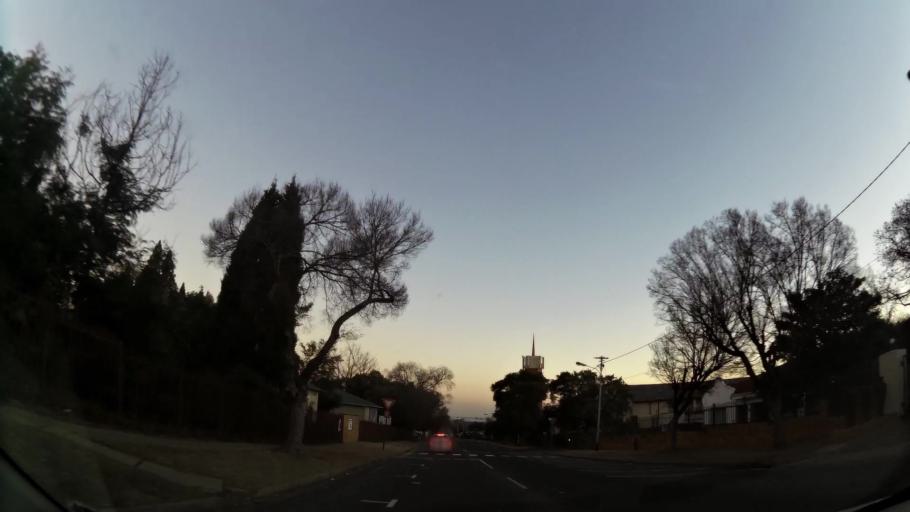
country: ZA
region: Gauteng
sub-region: City of Johannesburg Metropolitan Municipality
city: Roodepoort
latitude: -26.1720
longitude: 27.9239
